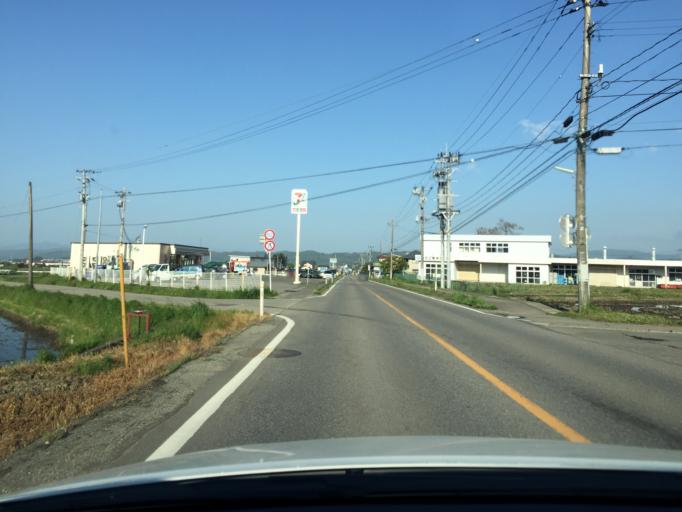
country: JP
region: Fukushima
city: Kitakata
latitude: 37.6568
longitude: 139.8965
